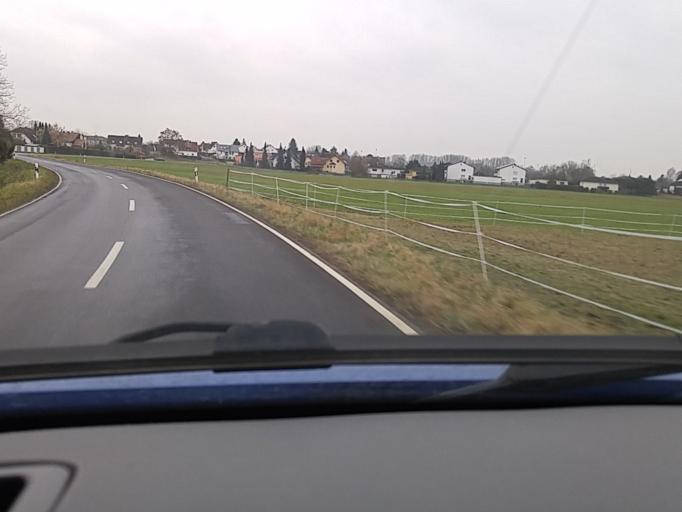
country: DE
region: Hesse
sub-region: Regierungsbezirk Darmstadt
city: Echzell
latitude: 50.3926
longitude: 8.8993
